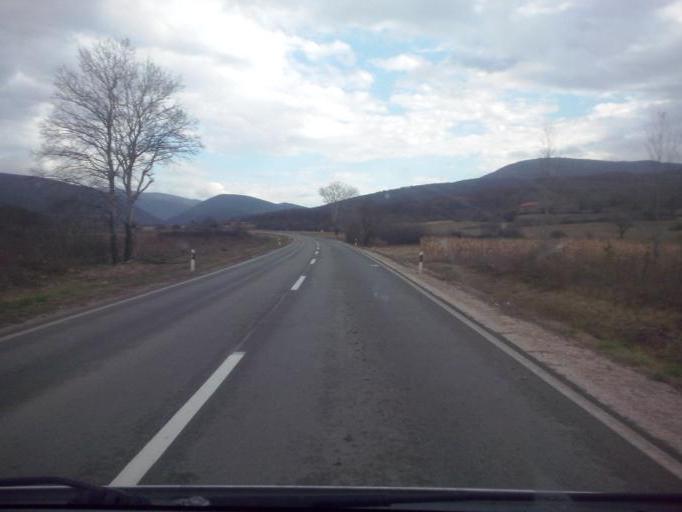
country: RS
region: Central Serbia
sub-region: Pomoravski Okrug
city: Paracin
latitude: 43.8544
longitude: 21.5759
